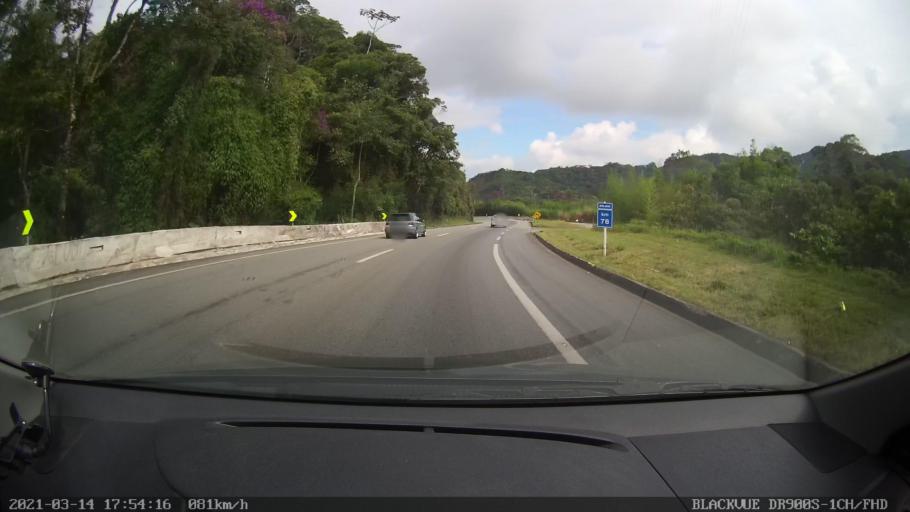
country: BR
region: Rio de Janeiro
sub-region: Petropolis
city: Petropolis
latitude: -22.4850
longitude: -43.2274
